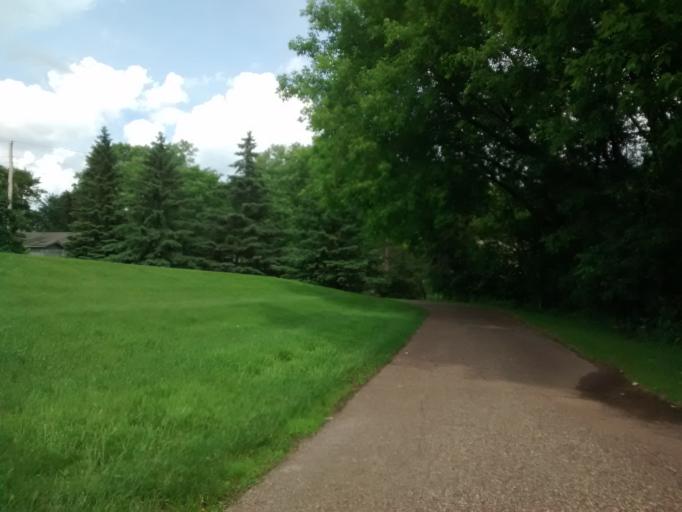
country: US
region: Minnesota
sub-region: Dakota County
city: Burnsville
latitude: 44.7545
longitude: -93.2936
